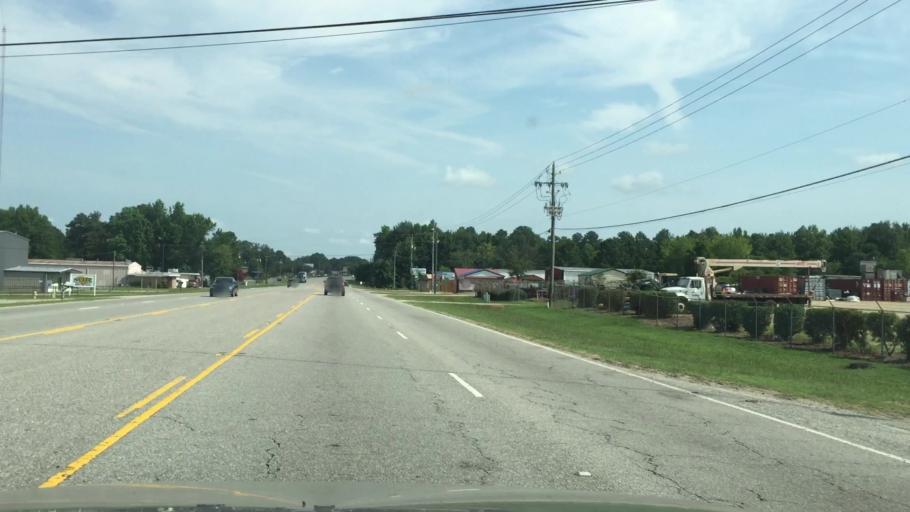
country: US
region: South Carolina
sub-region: Sumter County
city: South Sumter
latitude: 33.8947
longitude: -80.3522
